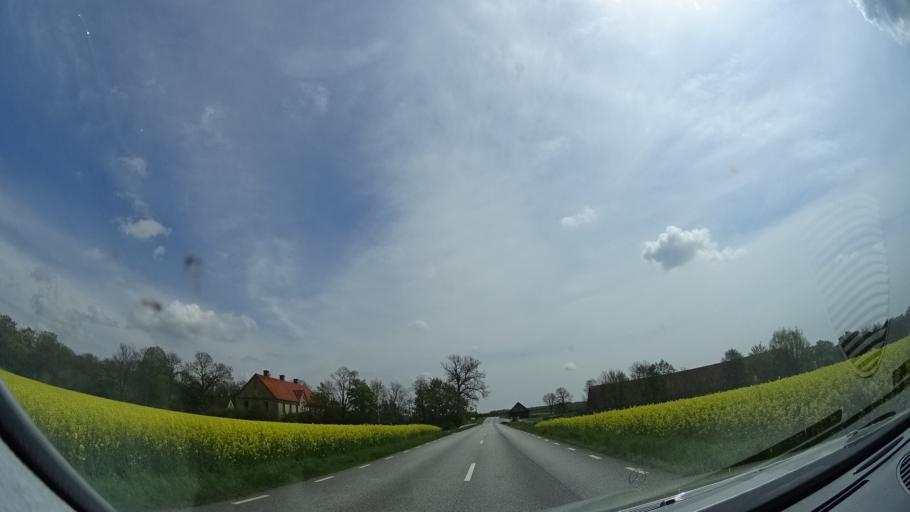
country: SE
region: Skane
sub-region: Sjobo Kommun
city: Blentarp
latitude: 55.6997
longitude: 13.5938
